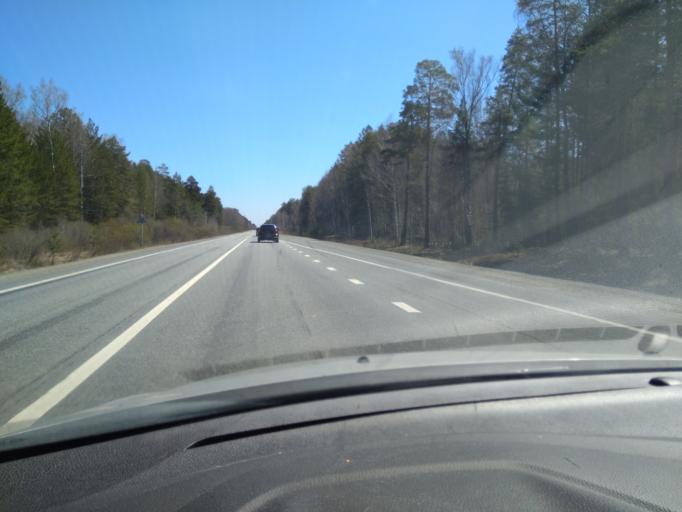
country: RU
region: Sverdlovsk
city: Yushala
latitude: 57.1112
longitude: 64.2682
